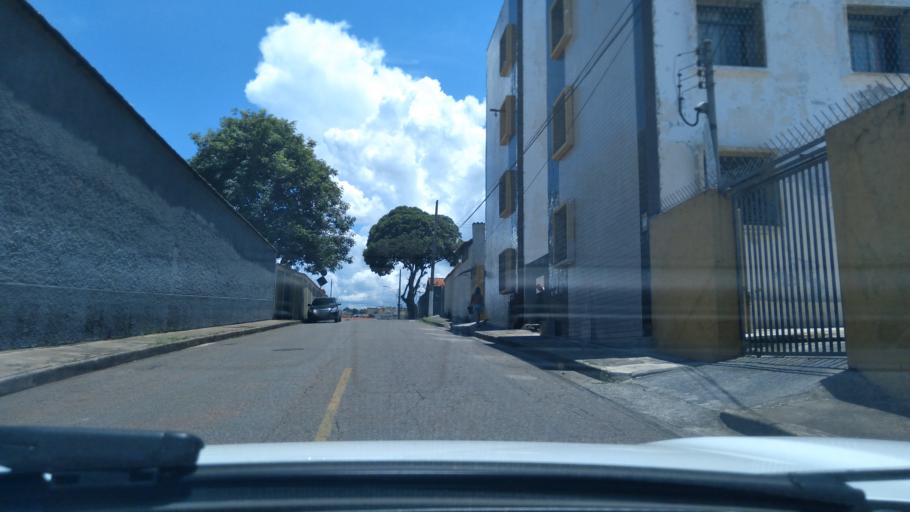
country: BR
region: Minas Gerais
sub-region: Contagem
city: Contagem
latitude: -19.9332
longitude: -43.9991
